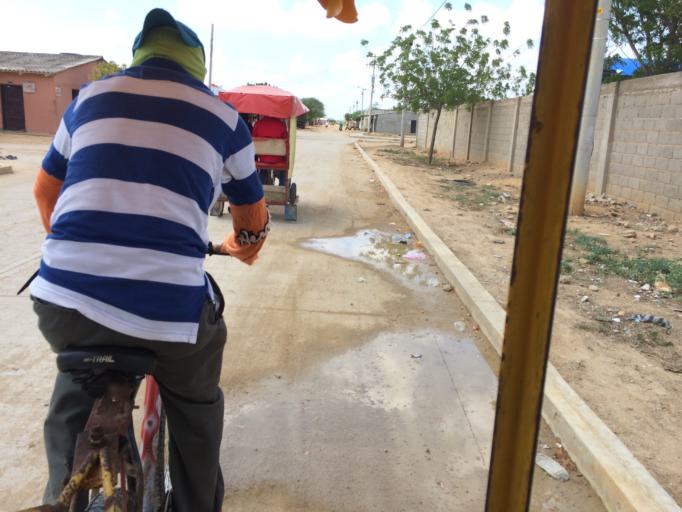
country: CO
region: La Guajira
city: Manaure
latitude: 11.7731
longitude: -72.4440
